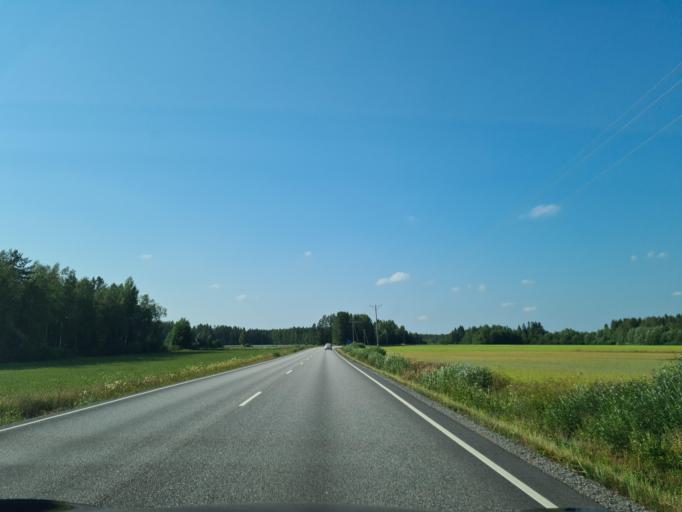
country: FI
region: Satakunta
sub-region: Pohjois-Satakunta
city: Karvia
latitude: 61.9617
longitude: 22.5107
